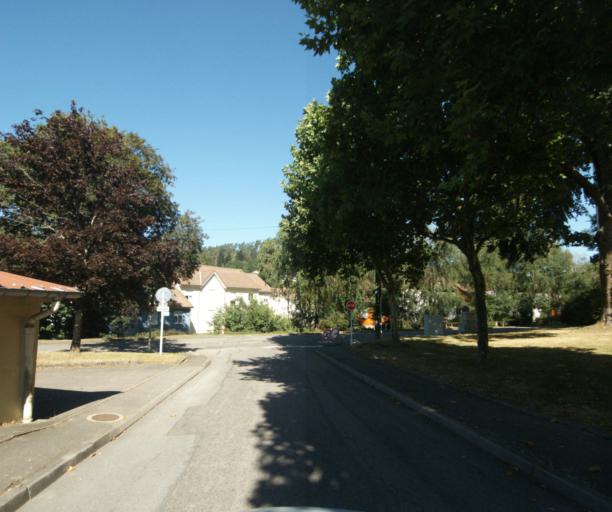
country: FR
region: Lorraine
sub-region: Departement des Vosges
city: Chantraine
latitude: 48.1528
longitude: 6.4522
